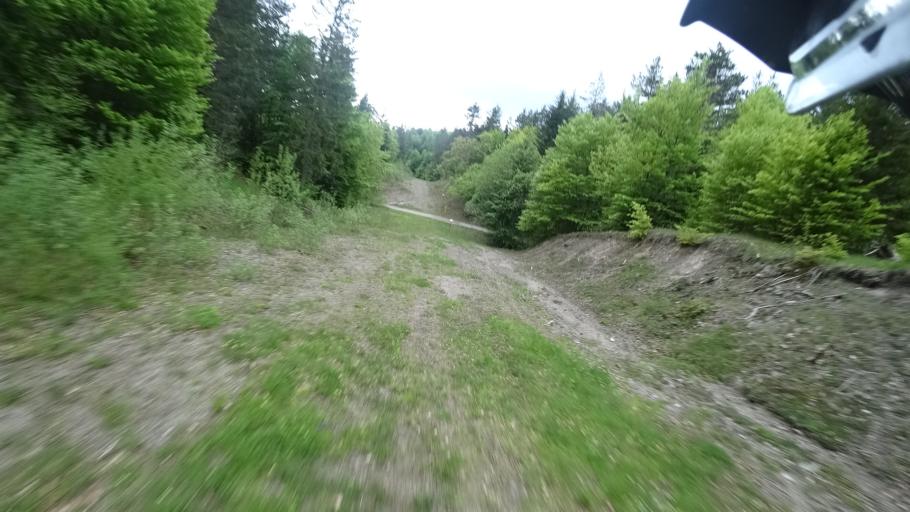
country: HR
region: Licko-Senjska
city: Jezerce
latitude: 44.8812
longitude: 15.4319
